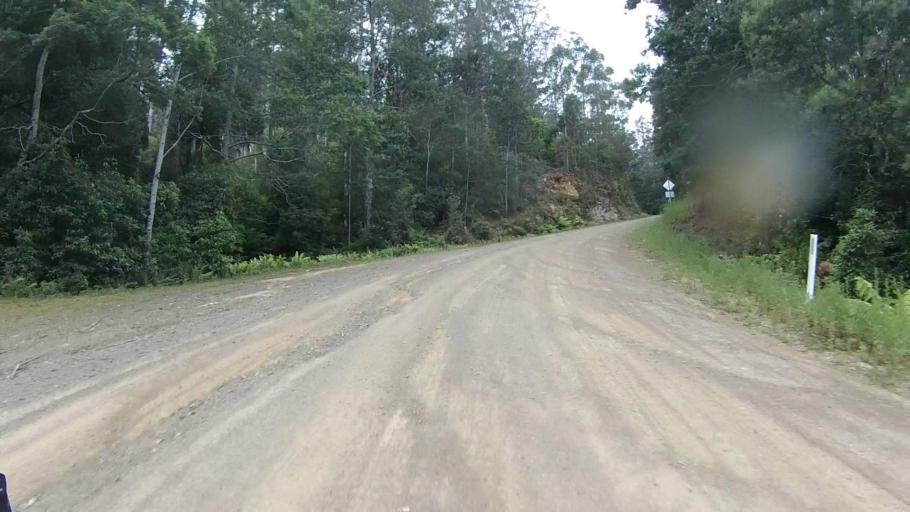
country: AU
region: Tasmania
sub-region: Sorell
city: Sorell
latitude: -42.7067
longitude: 147.8505
